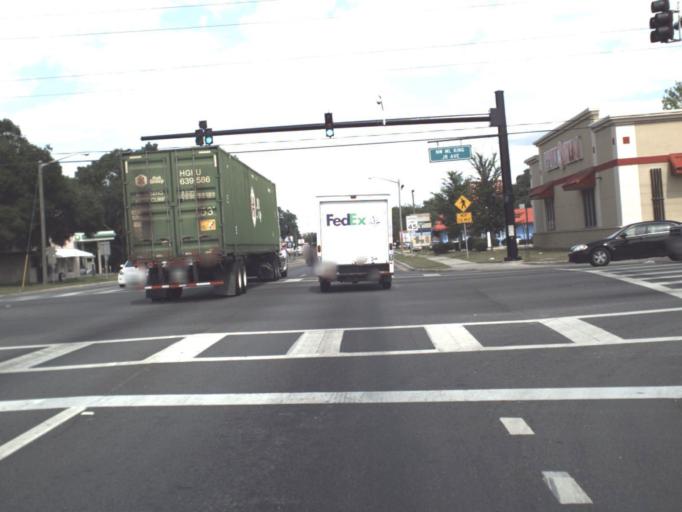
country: US
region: Florida
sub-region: Marion County
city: Ocala
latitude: 29.1969
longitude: -82.1527
